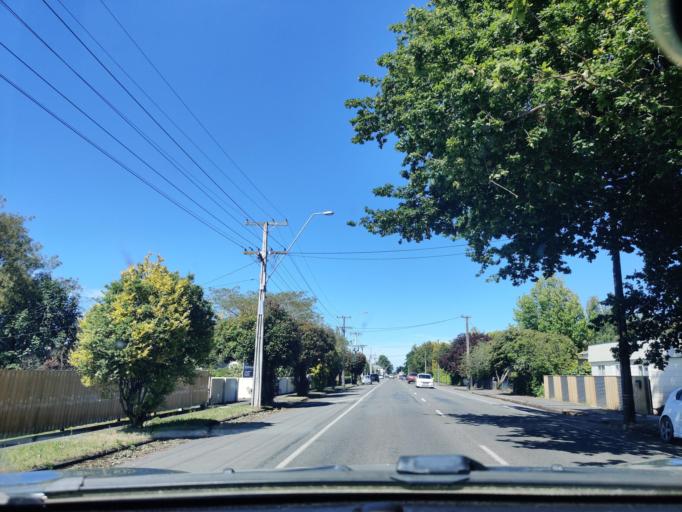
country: NZ
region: Wellington
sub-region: Masterton District
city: Masterton
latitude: -41.0753
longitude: 175.4661
